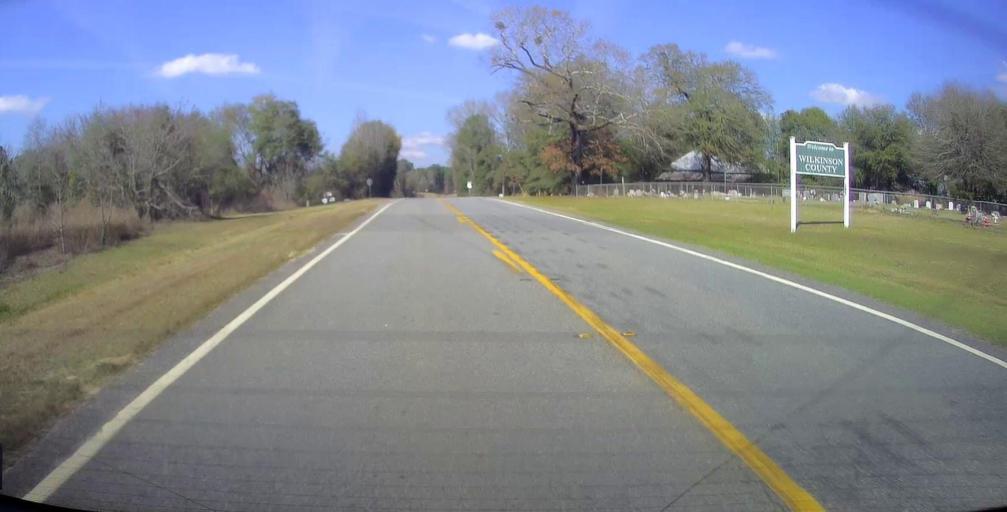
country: US
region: Georgia
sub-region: Twiggs County
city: Jeffersonville
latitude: 32.7745
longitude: -83.3332
